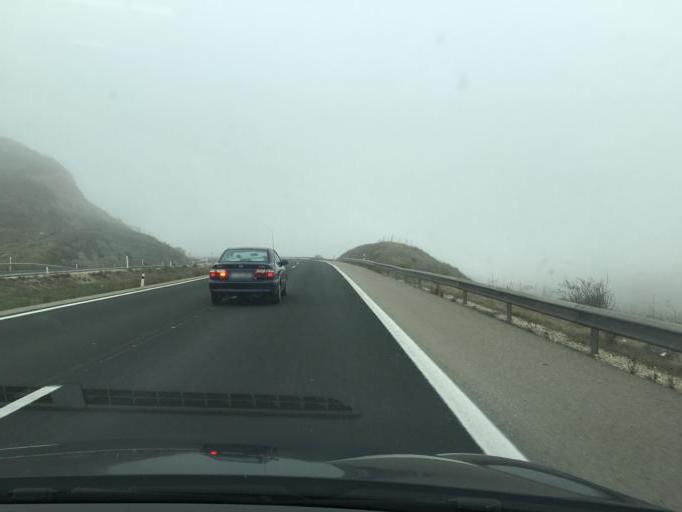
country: ES
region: Castille and Leon
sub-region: Provincia de Burgos
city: Pancorbo
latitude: 42.6233
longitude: -3.1338
